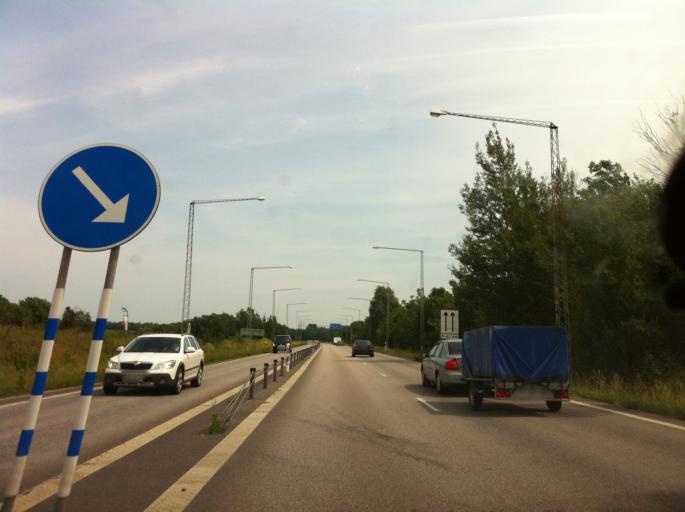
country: SE
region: Kalmar
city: Faerjestaden
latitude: 56.6665
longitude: 16.4866
